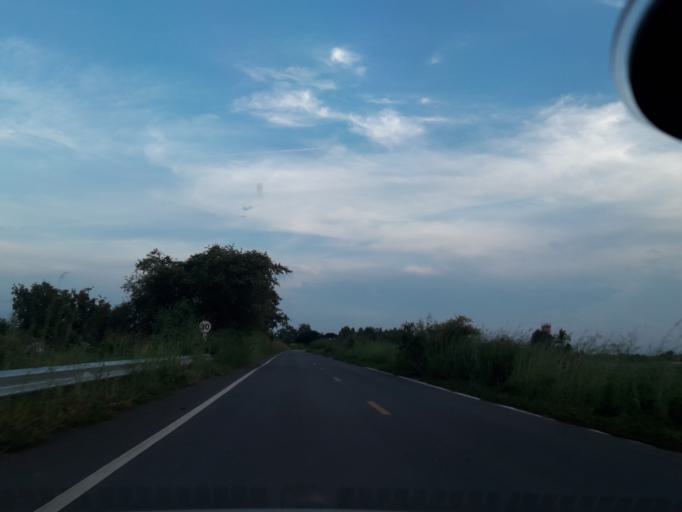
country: TH
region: Sara Buri
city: Nong Khae
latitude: 14.3026
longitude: 100.8892
